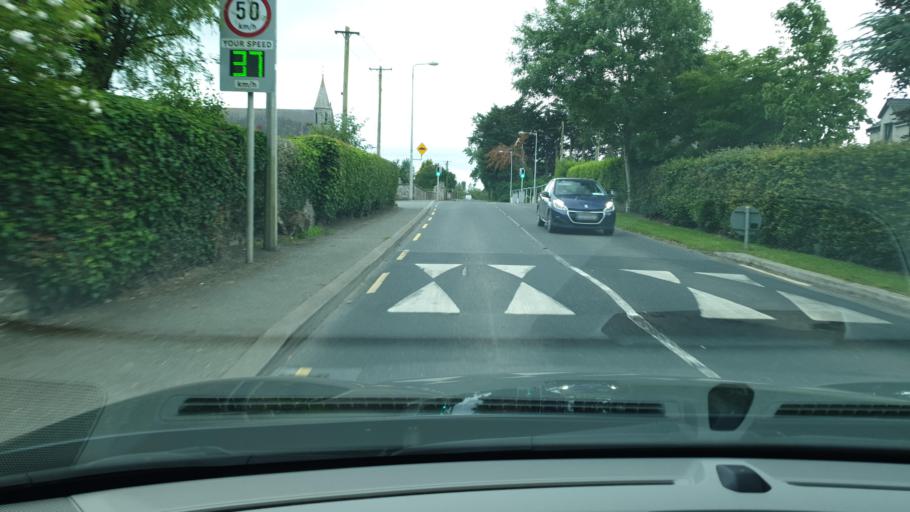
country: IE
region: Leinster
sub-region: An Mhi
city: Ratoath
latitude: 53.5385
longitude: -6.4432
